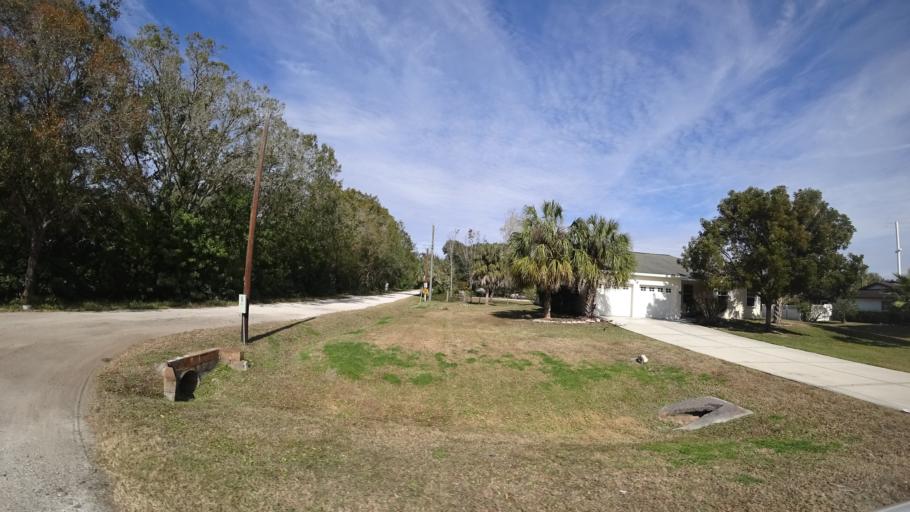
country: US
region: Florida
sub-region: Manatee County
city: Ellenton
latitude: 27.5137
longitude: -82.4069
